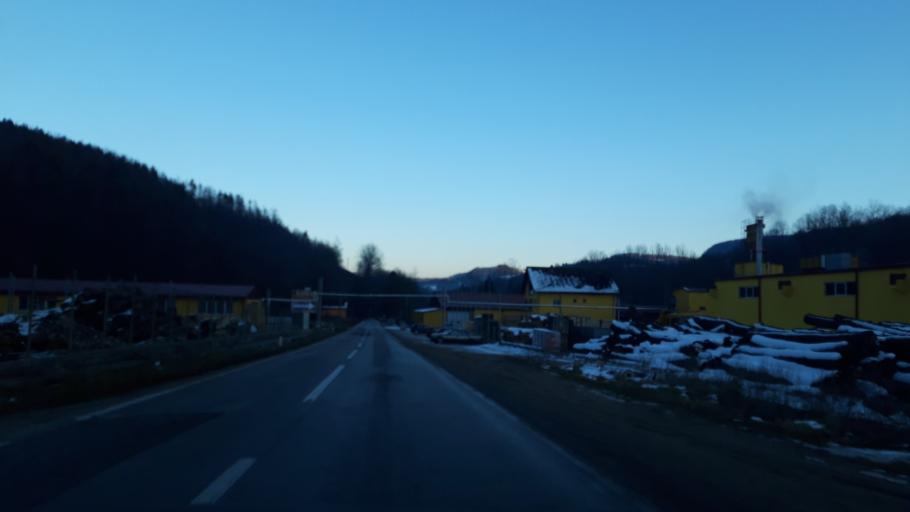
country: BA
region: Republika Srpska
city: Milici
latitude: 44.1661
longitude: 19.0363
